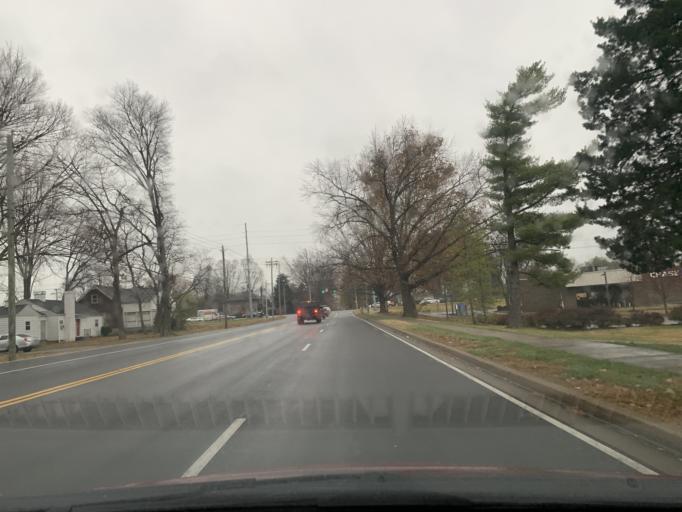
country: US
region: Kentucky
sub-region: Jefferson County
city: West Buechel
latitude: 38.2022
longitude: -85.6659
